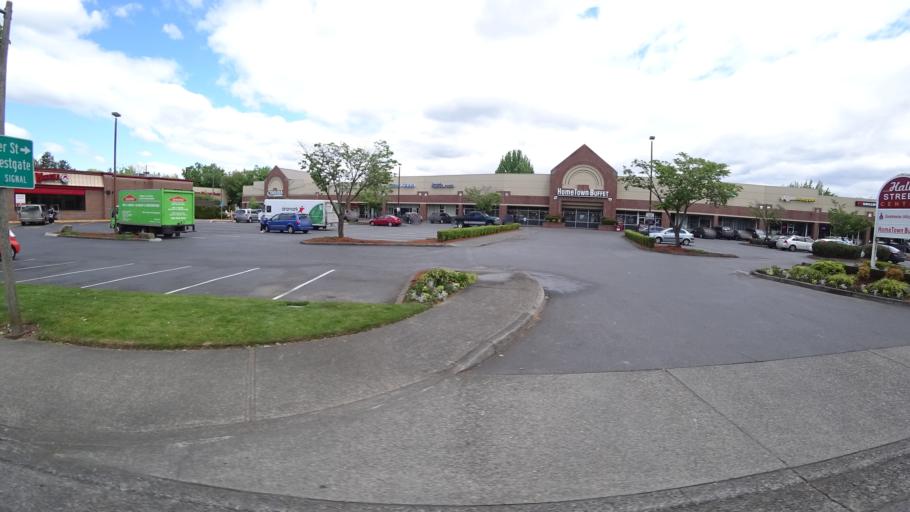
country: US
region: Oregon
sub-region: Washington County
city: Beaverton
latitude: 45.4923
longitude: -122.8062
